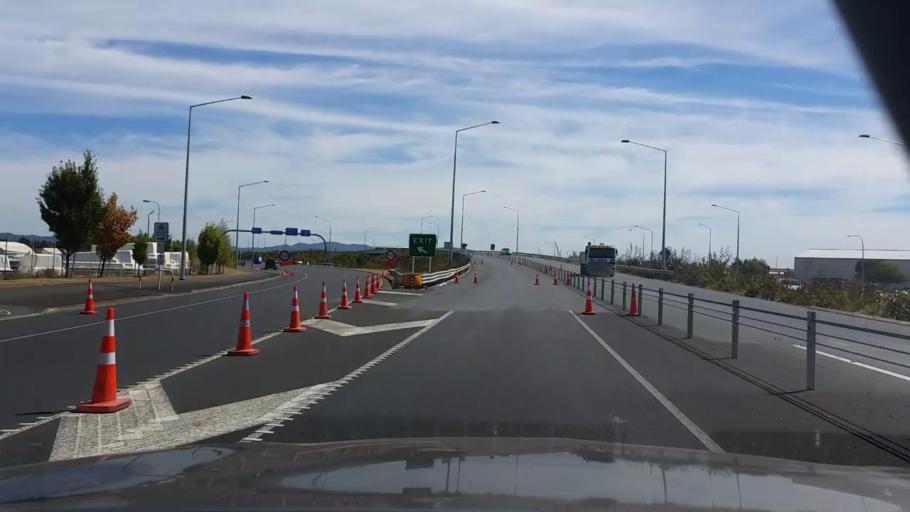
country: NZ
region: Waikato
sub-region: Hamilton City
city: Hamilton
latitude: -37.7578
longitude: 175.2314
